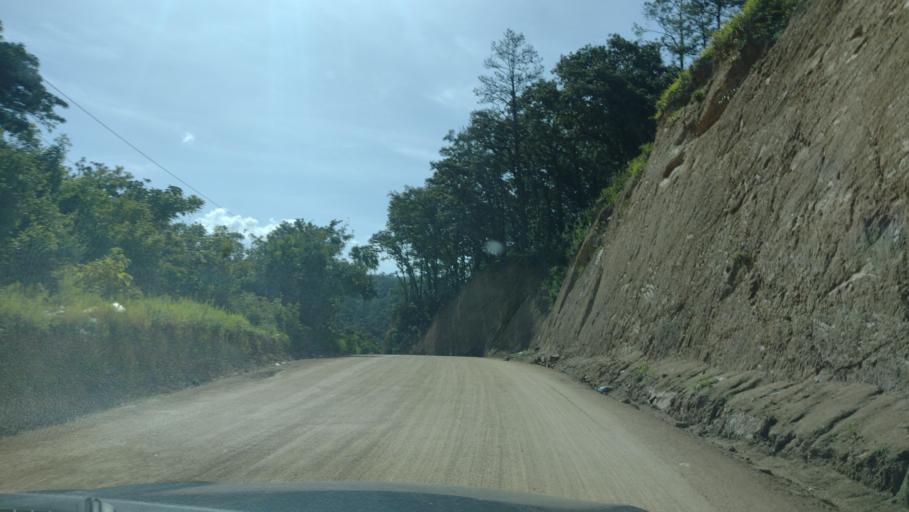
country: GT
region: Guatemala
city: Chinautla
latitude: 14.7552
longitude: -90.5152
